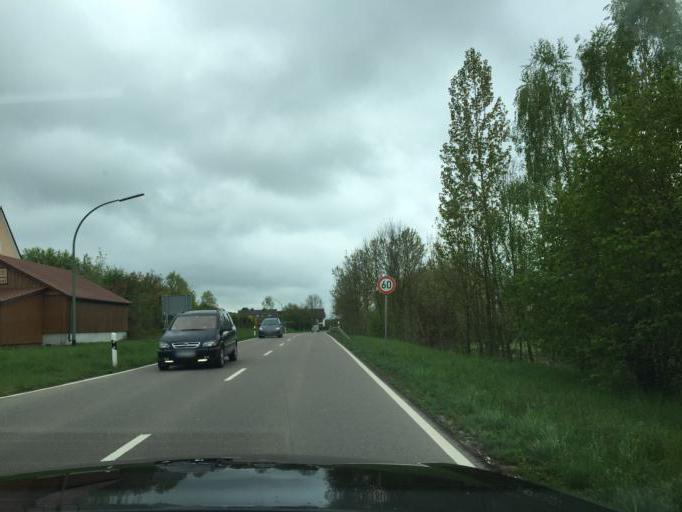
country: DE
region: Bavaria
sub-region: Swabia
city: Buttenwiesen
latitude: 48.5862
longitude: 10.7185
